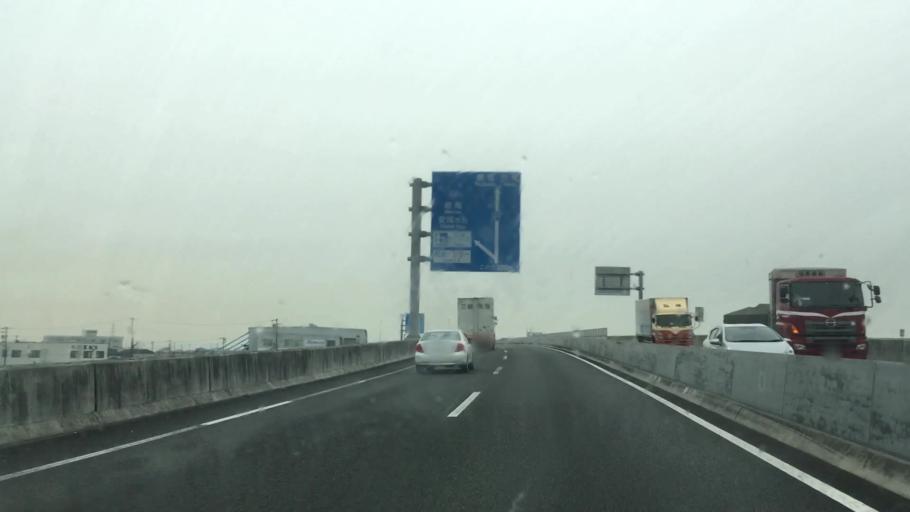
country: JP
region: Aichi
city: Anjo
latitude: 34.9338
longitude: 137.0434
